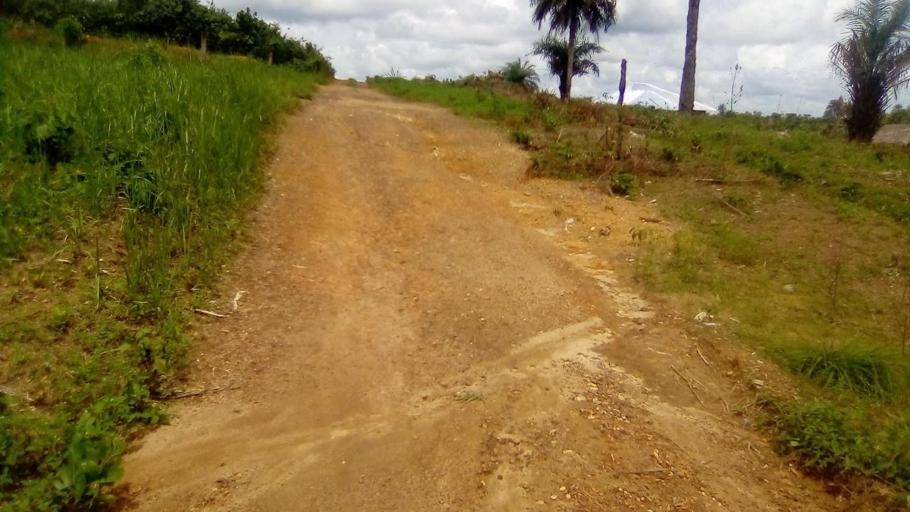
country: SL
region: Southern Province
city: Bo
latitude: 7.9275
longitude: -11.7486
